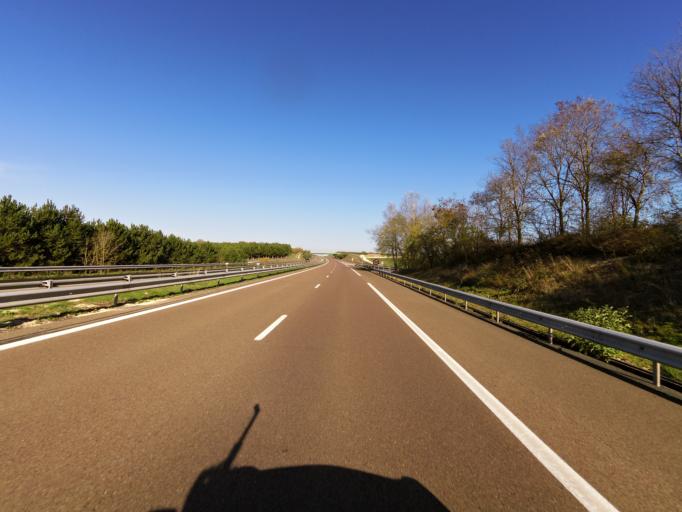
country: FR
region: Champagne-Ardenne
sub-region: Departement de la Marne
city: Compertrix
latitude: 48.8866
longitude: 4.2901
